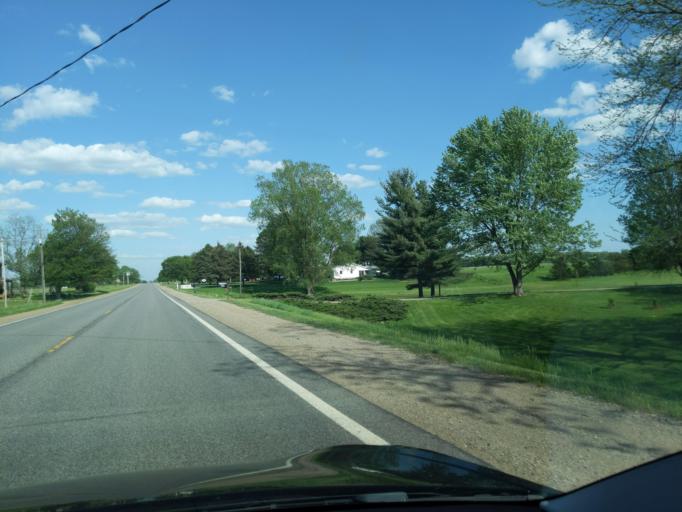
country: US
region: Michigan
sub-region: Ionia County
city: Portland
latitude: 42.7556
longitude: -84.9302
